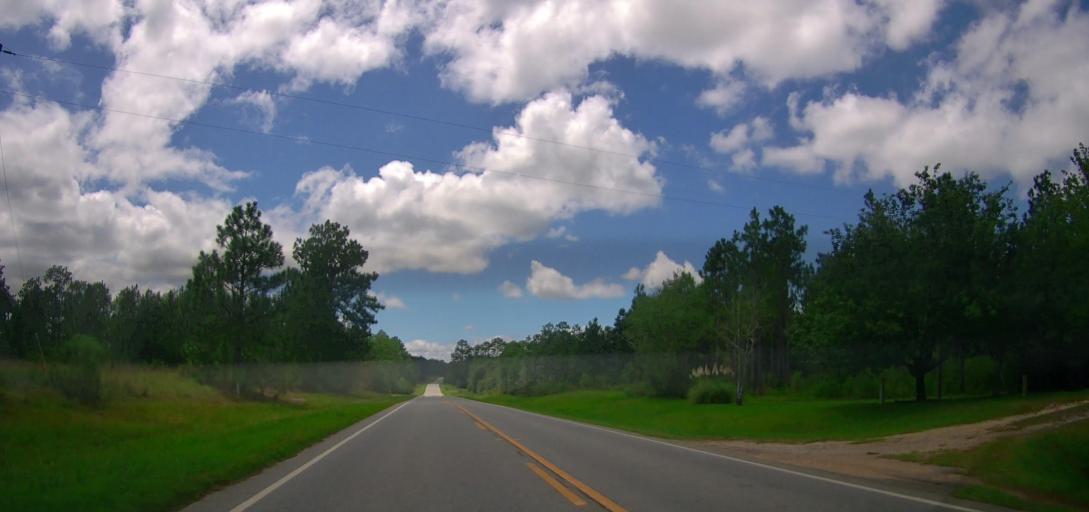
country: US
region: Georgia
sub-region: Turner County
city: Ashburn
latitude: 31.7224
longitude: -83.5713
